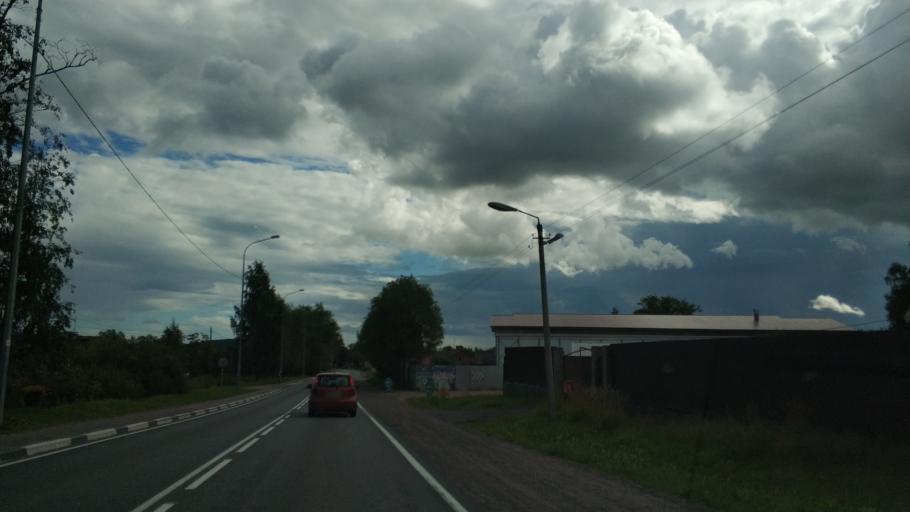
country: RU
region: Republic of Karelia
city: Khelyulya
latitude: 61.7528
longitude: 30.6595
